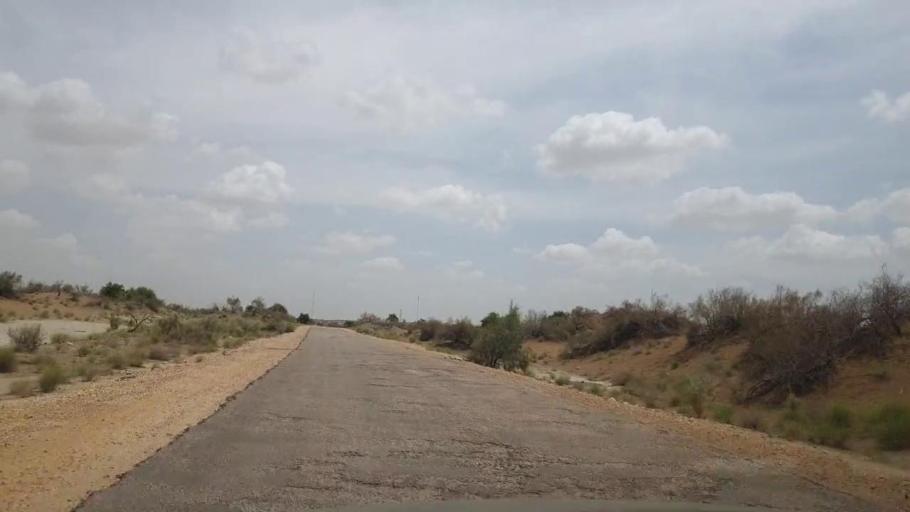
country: PK
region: Sindh
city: Kot Diji
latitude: 27.1428
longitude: 69.2246
